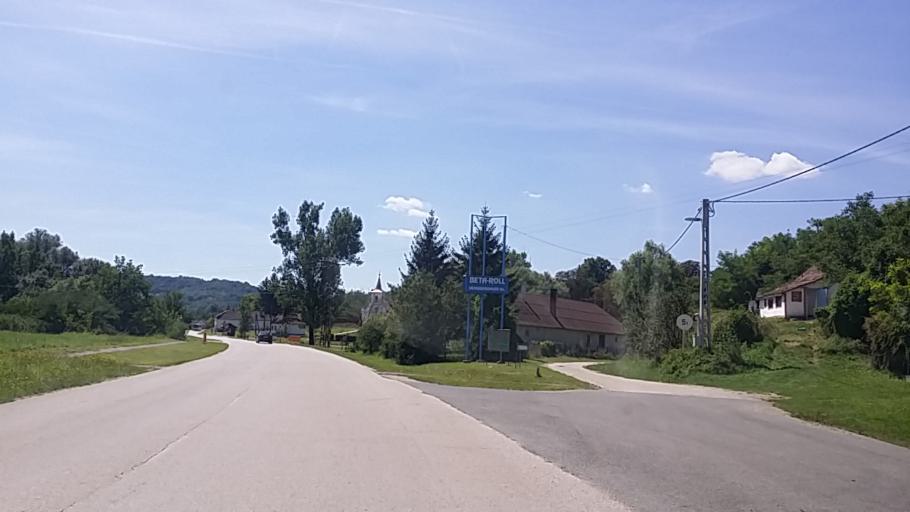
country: HU
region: Tolna
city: Iregszemcse
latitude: 46.7564
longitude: 18.1250
